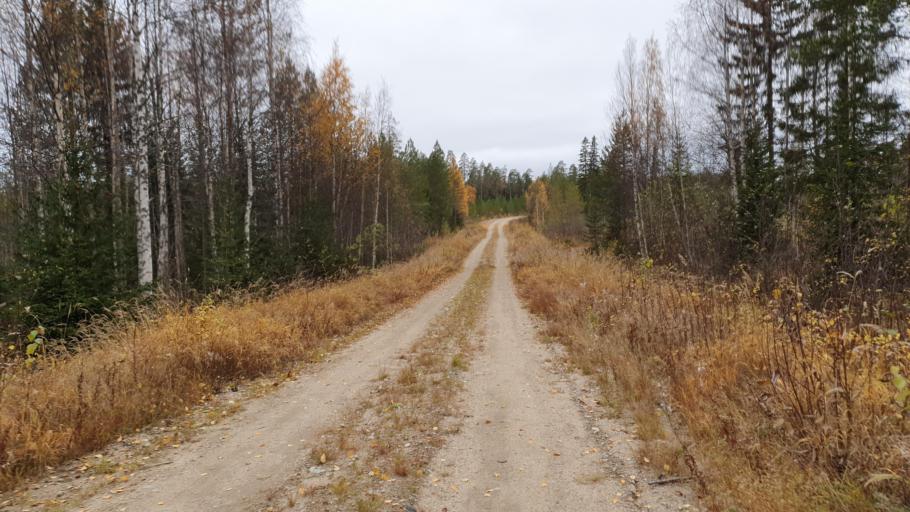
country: FI
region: Kainuu
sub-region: Kehys-Kainuu
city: Kuhmo
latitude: 64.4392
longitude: 29.6275
